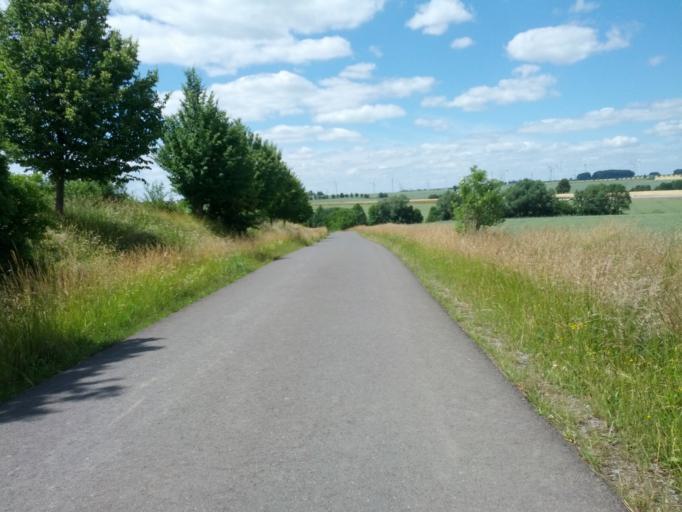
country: DE
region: Thuringia
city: Bischofroda
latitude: 51.0121
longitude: 10.3584
